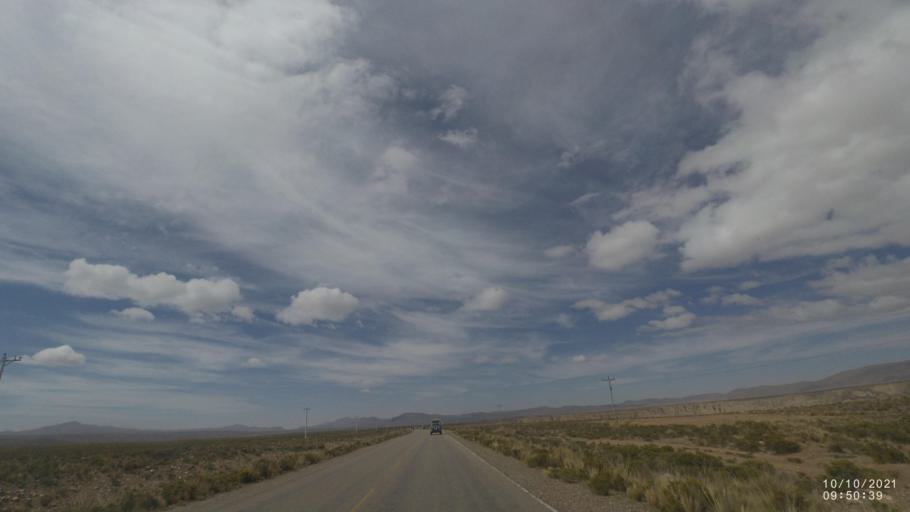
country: BO
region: La Paz
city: Colquiri
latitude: -17.2468
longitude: -67.3329
